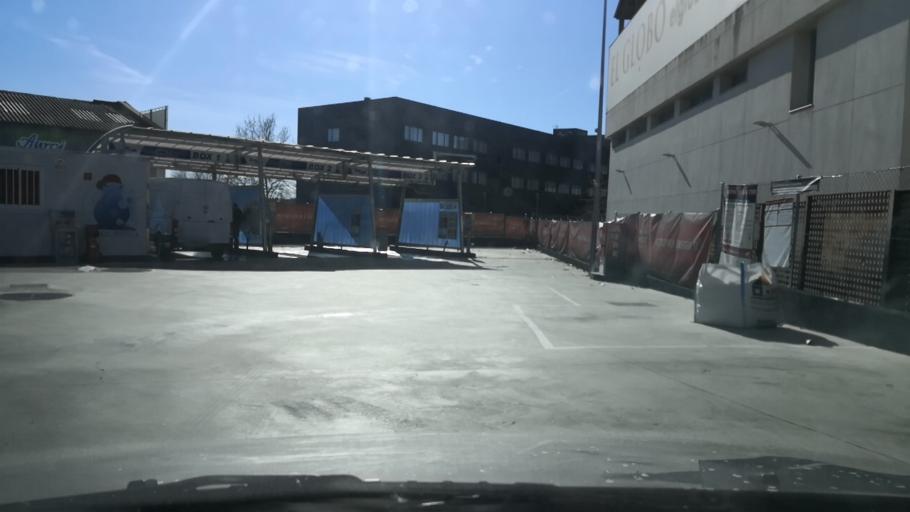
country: ES
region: Madrid
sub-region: Provincia de Madrid
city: San Sebastian de los Reyes
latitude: 40.5477
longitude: -3.6125
